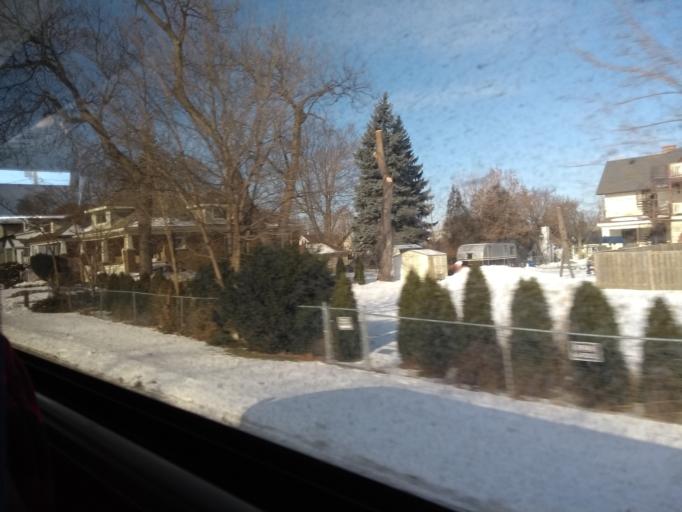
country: CA
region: Ontario
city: Niagara Falls
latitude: 43.1086
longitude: -79.0840
